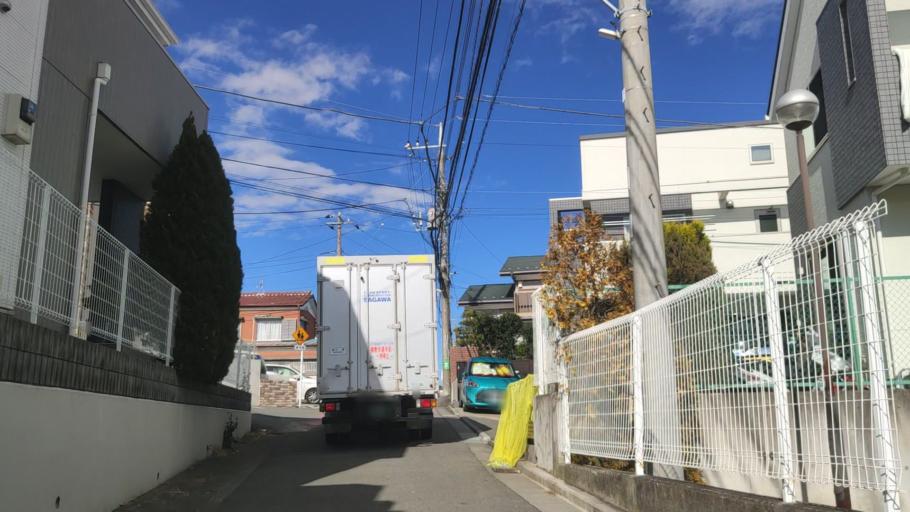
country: JP
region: Kanagawa
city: Yokohama
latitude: 35.4734
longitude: 139.5811
